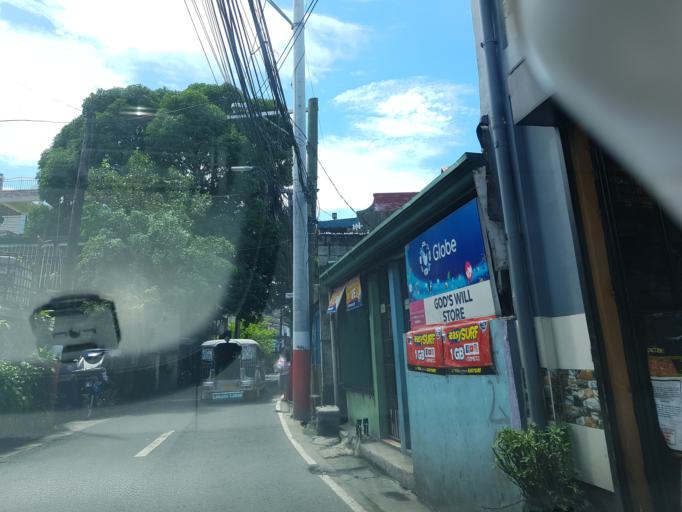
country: PH
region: Calabarzon
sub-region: Province of Rizal
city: Taguig
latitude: 14.5267
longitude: 121.0724
